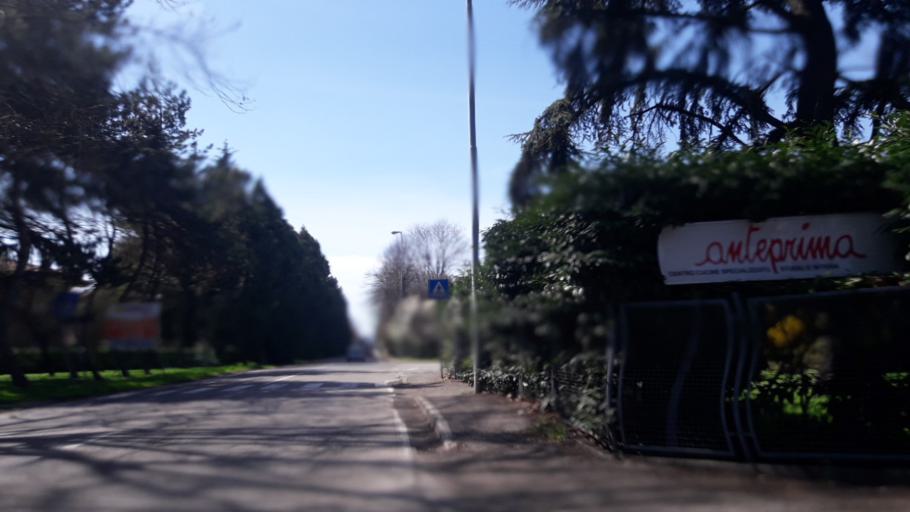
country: IT
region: Emilia-Romagna
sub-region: Provincia di Reggio Emilia
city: Reggio nell'Emilia
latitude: 44.6735
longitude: 10.6110
